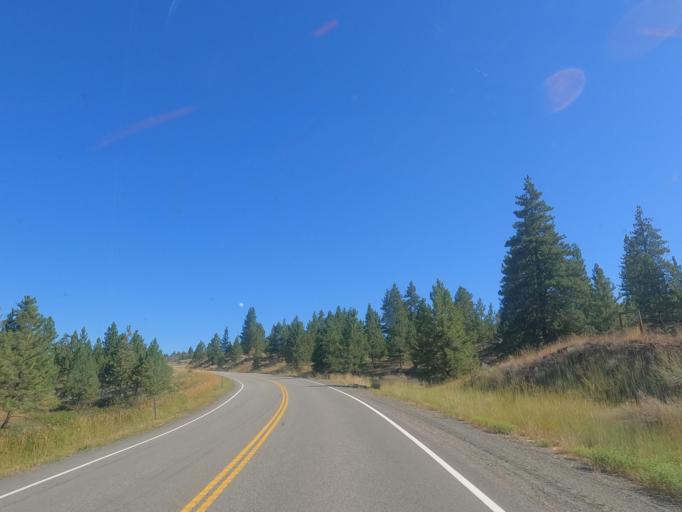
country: CA
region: British Columbia
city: Merritt
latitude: 50.1838
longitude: -120.8531
